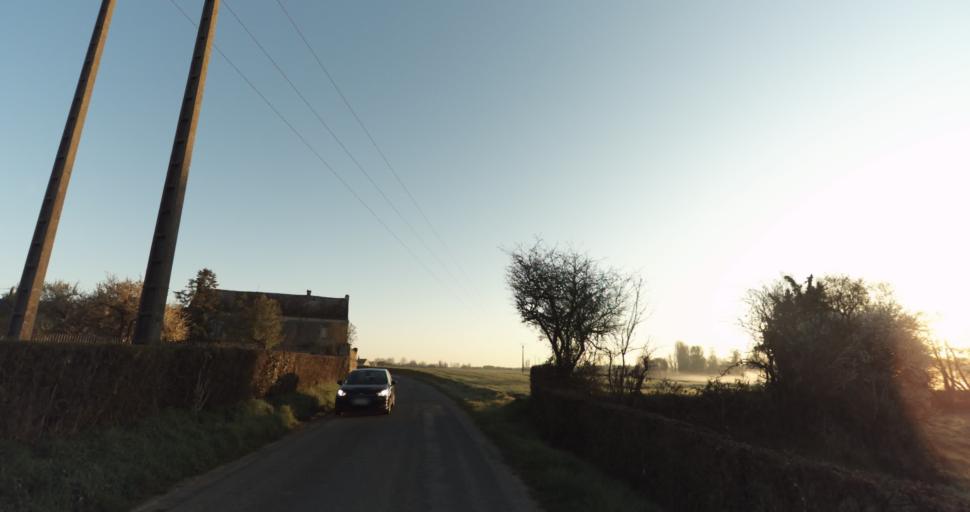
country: FR
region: Lower Normandy
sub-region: Departement du Calvados
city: Saint-Pierre-sur-Dives
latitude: 49.0287
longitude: -0.0322
